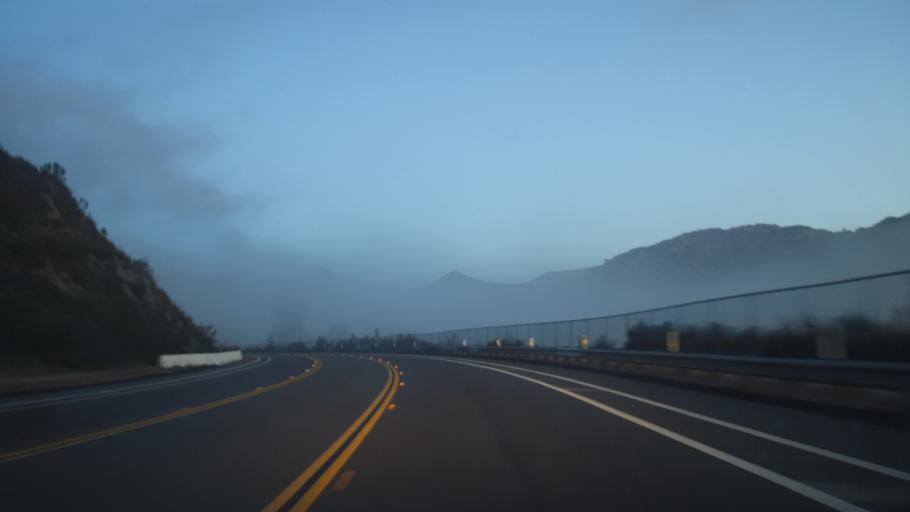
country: US
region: California
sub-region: San Diego County
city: Granite Hills
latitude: 32.7803
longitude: -116.8880
